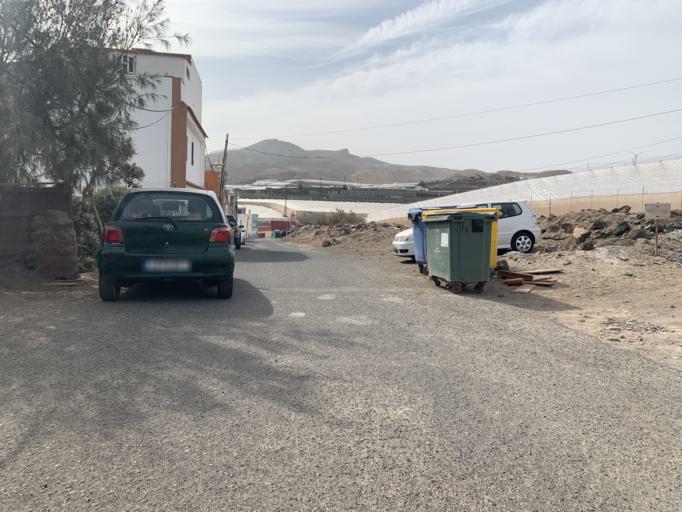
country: ES
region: Canary Islands
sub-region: Provincia de Las Palmas
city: Galdar
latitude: 28.1590
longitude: -15.6710
